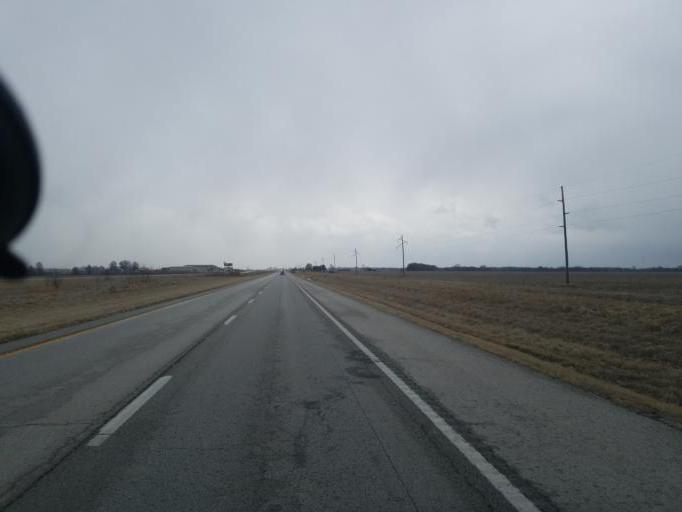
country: US
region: Missouri
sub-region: Randolph County
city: Moberly
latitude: 39.5501
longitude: -92.4544
